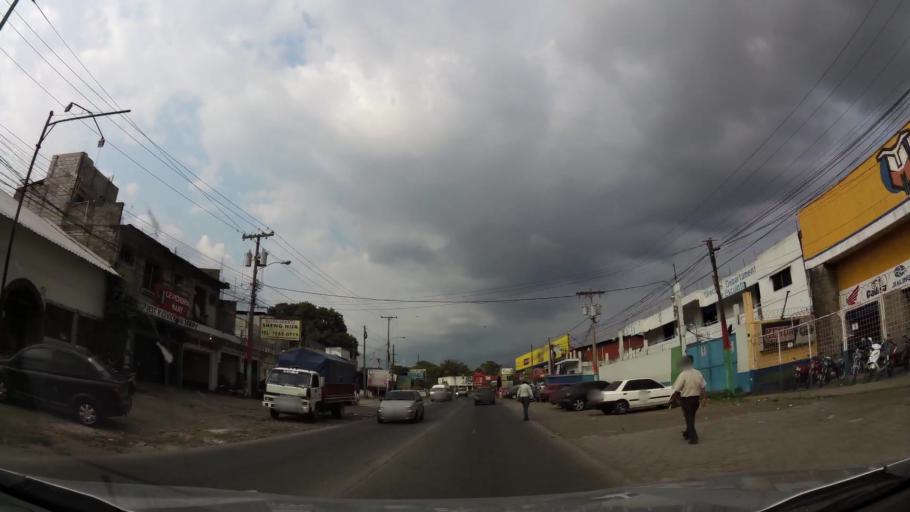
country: GT
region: Escuintla
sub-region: Municipio de Escuintla
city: Escuintla
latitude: 14.3006
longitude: -90.7813
